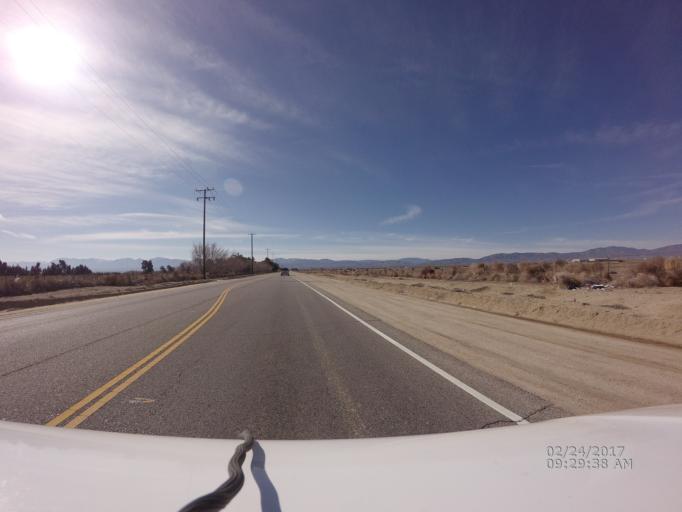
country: US
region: California
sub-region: Los Angeles County
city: Palmdale
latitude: 34.6310
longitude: -118.0409
